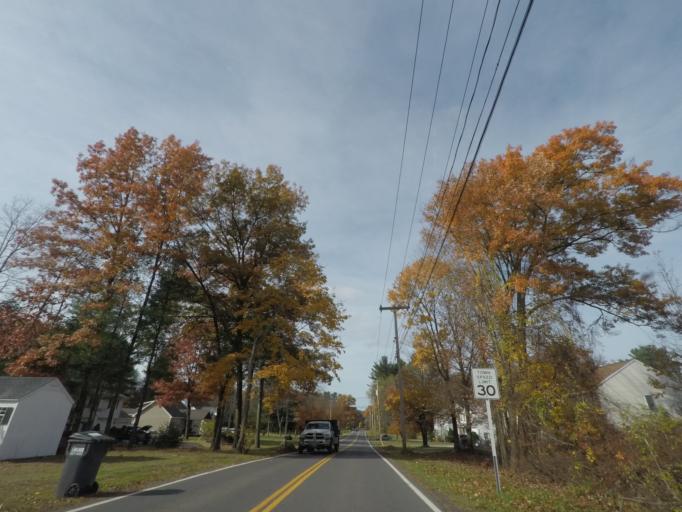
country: US
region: New York
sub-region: Schenectady County
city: Rotterdam
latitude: 42.7523
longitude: -73.9544
